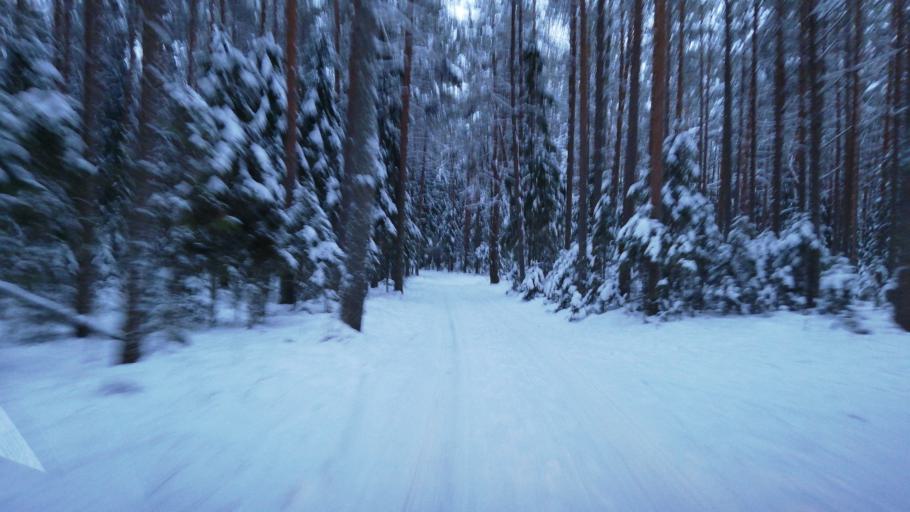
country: RU
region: Jaroslavl
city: Krasnyye Tkachi
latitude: 57.4474
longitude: 39.7972
